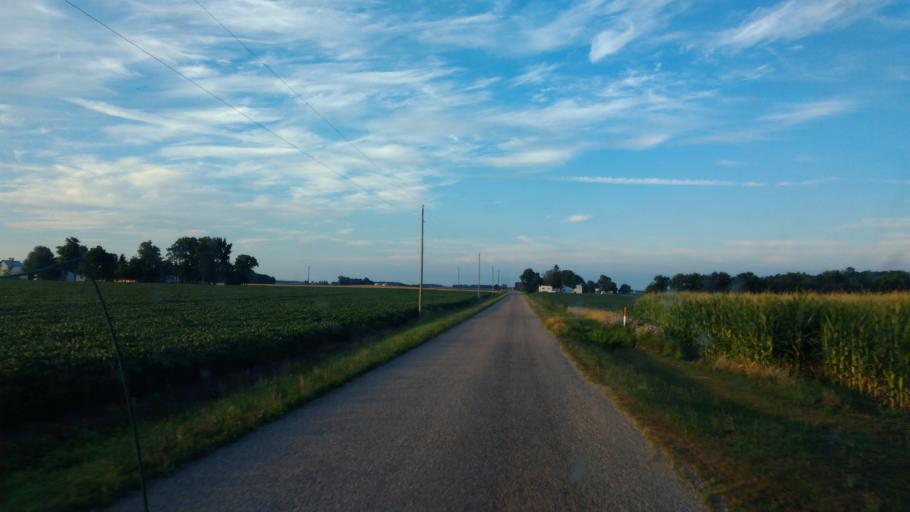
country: US
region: Indiana
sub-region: Adams County
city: Berne
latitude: 40.6510
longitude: -85.0608
